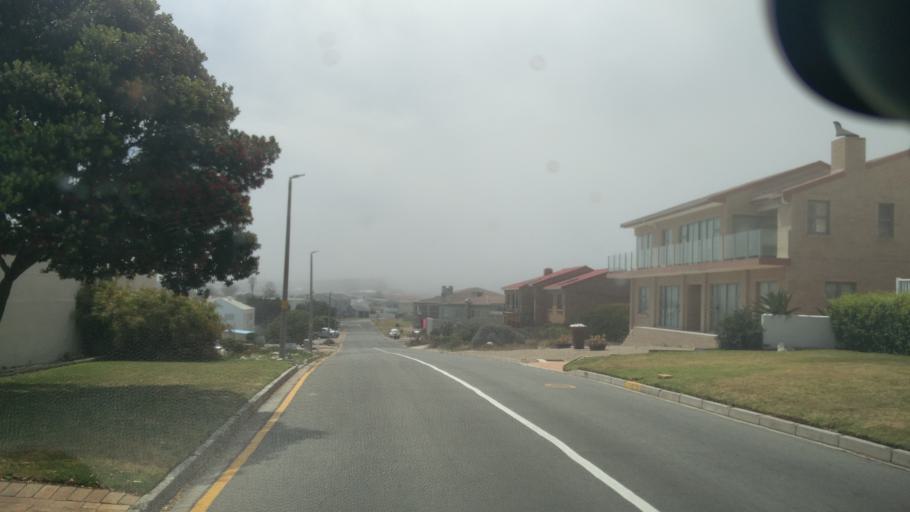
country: ZA
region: Western Cape
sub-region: West Coast District Municipality
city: Saldanha
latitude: -33.3483
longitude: 18.1512
